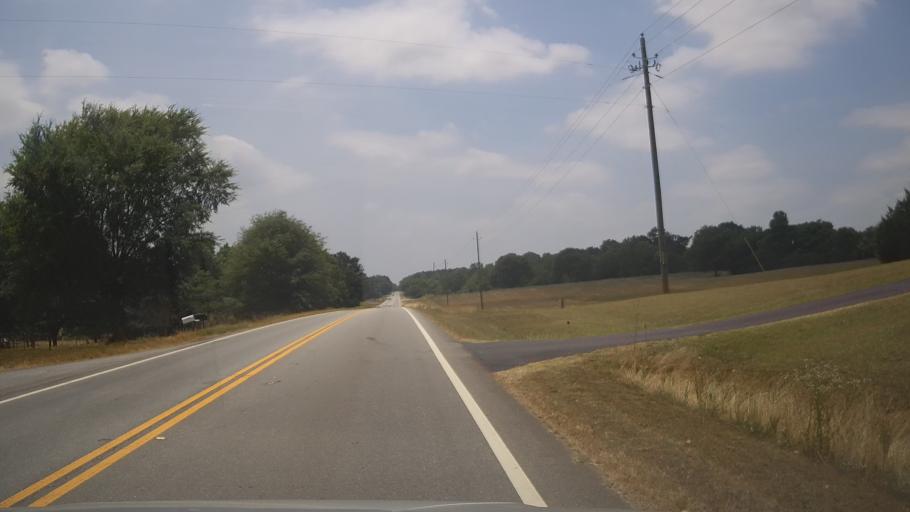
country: US
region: Georgia
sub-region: Jackson County
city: Nicholson
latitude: 34.1797
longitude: -83.3560
